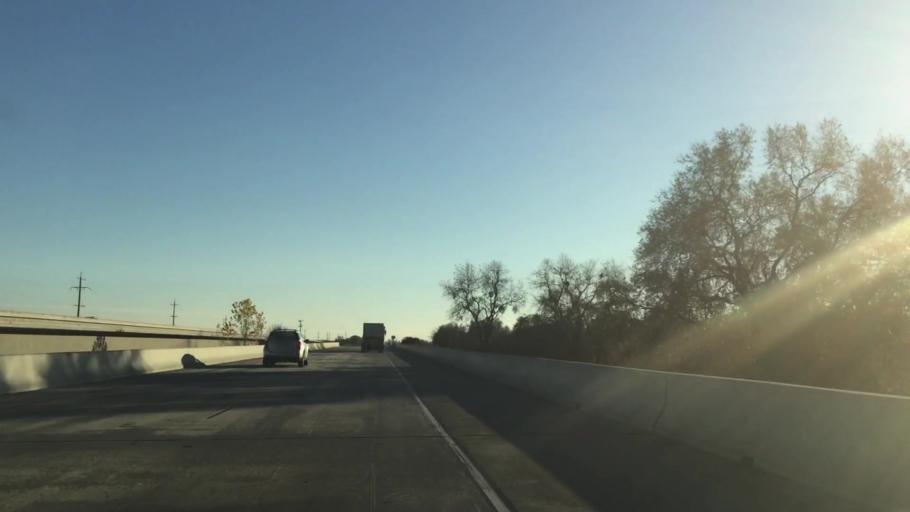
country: US
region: California
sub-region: Yuba County
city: Plumas Lake
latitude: 38.9709
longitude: -121.5434
